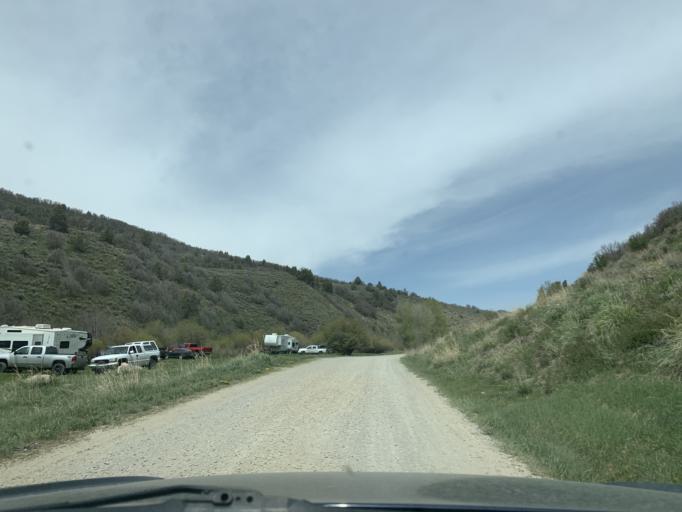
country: US
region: Utah
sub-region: Utah County
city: Mapleton
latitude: 40.1652
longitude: -111.3299
